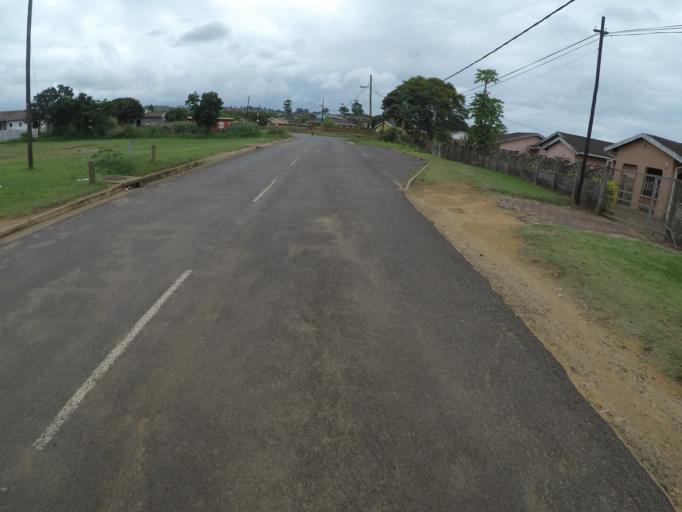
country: ZA
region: KwaZulu-Natal
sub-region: uThungulu District Municipality
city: Empangeni
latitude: -28.7802
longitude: 31.8500
